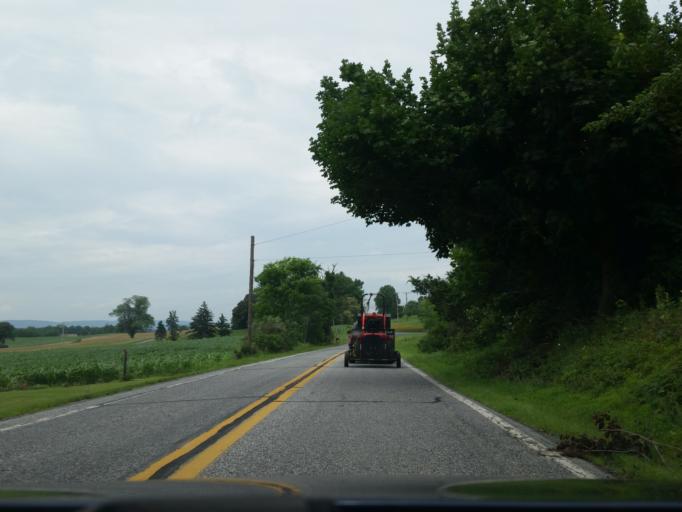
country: US
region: Pennsylvania
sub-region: Lebanon County
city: Palmyra
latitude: 40.3943
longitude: -76.6037
